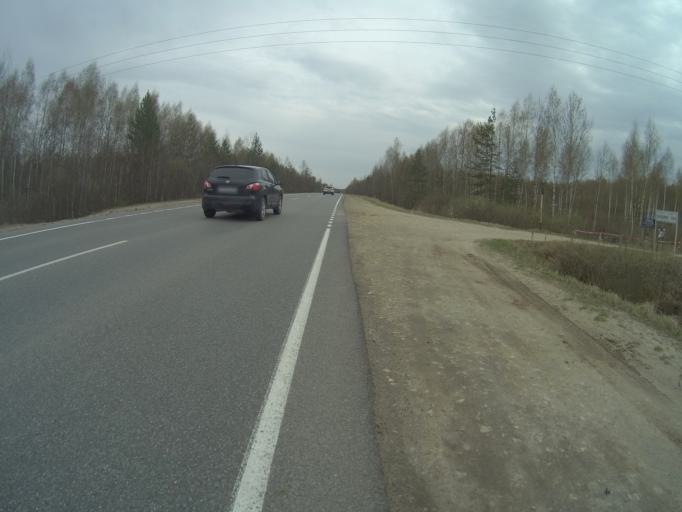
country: RU
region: Vladimir
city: Golovino
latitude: 55.9617
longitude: 40.5582
